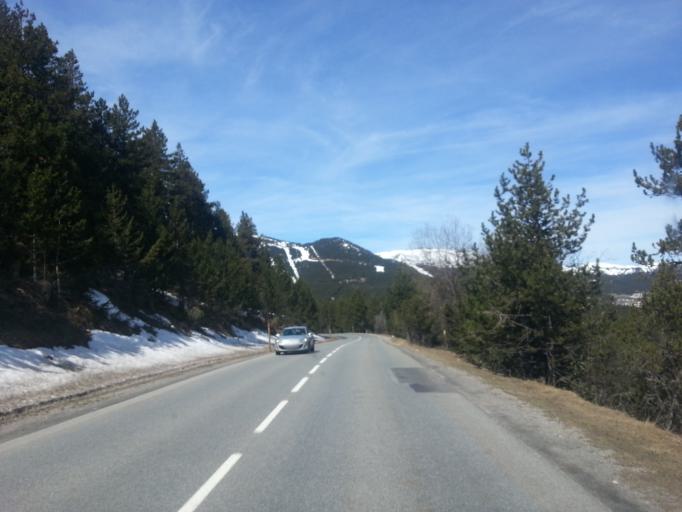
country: ES
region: Catalonia
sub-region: Provincia de Girona
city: Llivia
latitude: 42.5519
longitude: 2.0840
